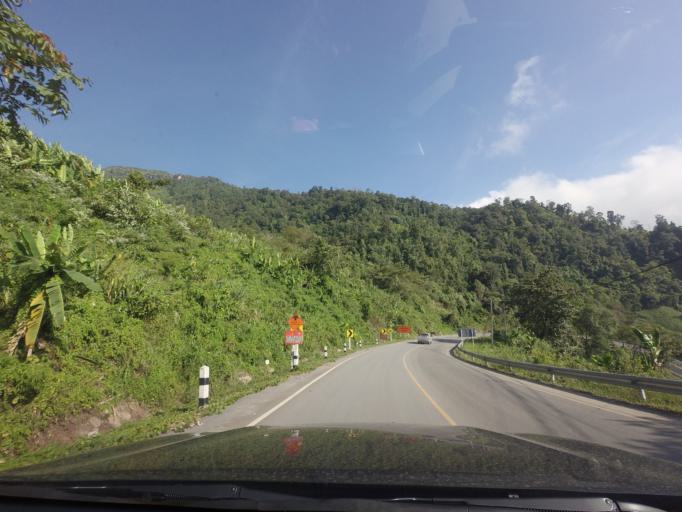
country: TH
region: Phetchabun
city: Lom Kao
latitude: 16.8863
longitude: 101.1203
